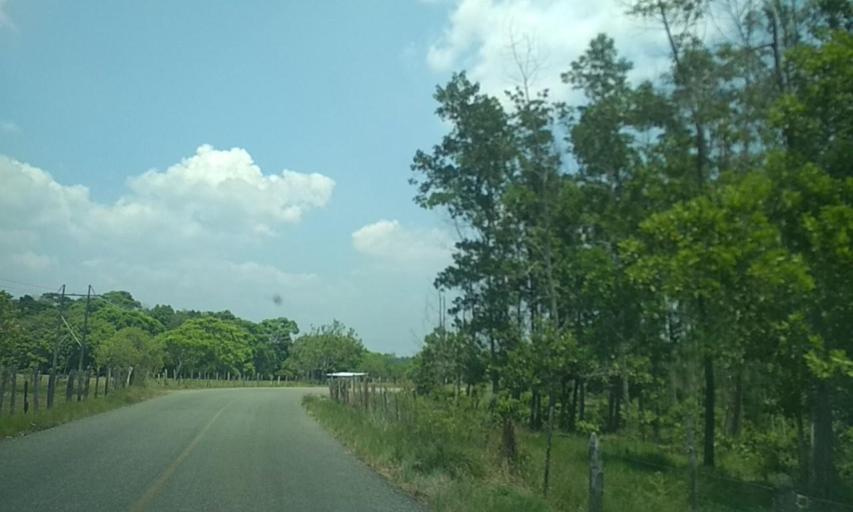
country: MX
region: Tabasco
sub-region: Huimanguillo
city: Francisco Rueda
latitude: 17.8382
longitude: -93.9100
